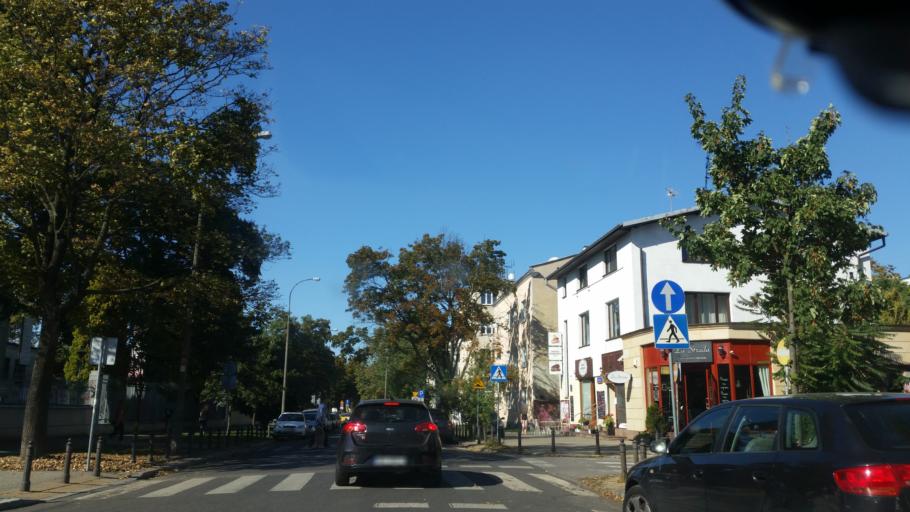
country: PL
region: Masovian Voivodeship
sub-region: Warszawa
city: Zoliborz
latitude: 52.2673
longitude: 20.9849
